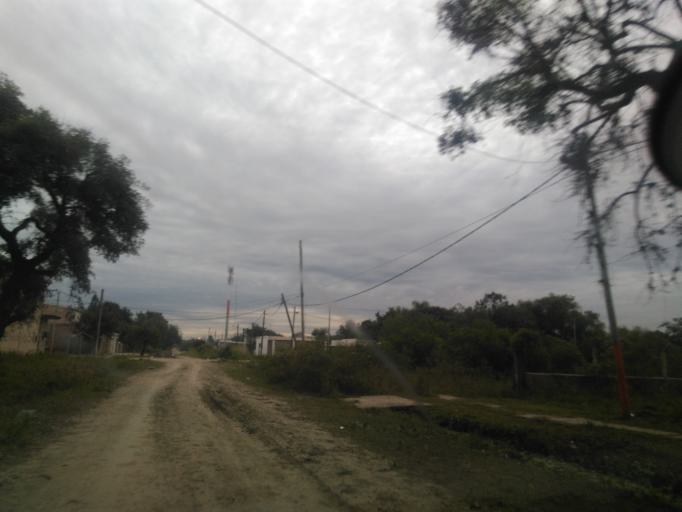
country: AR
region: Chaco
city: Resistencia
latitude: -27.4708
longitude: -59.0118
